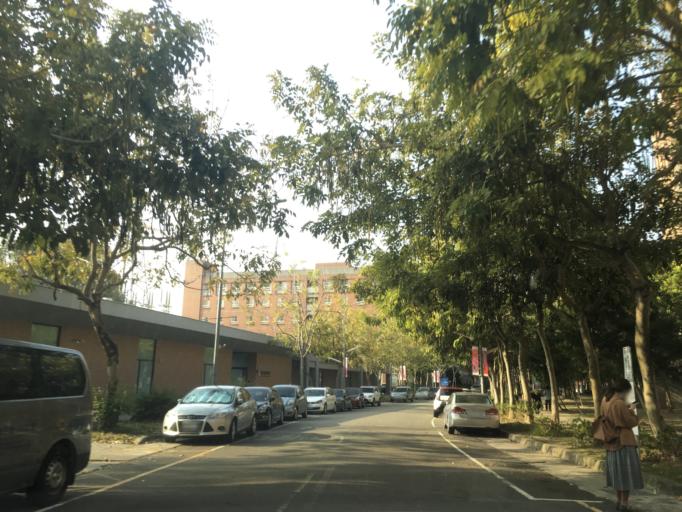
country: TW
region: Taiwan
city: Zhongxing New Village
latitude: 24.0457
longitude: 120.6852
